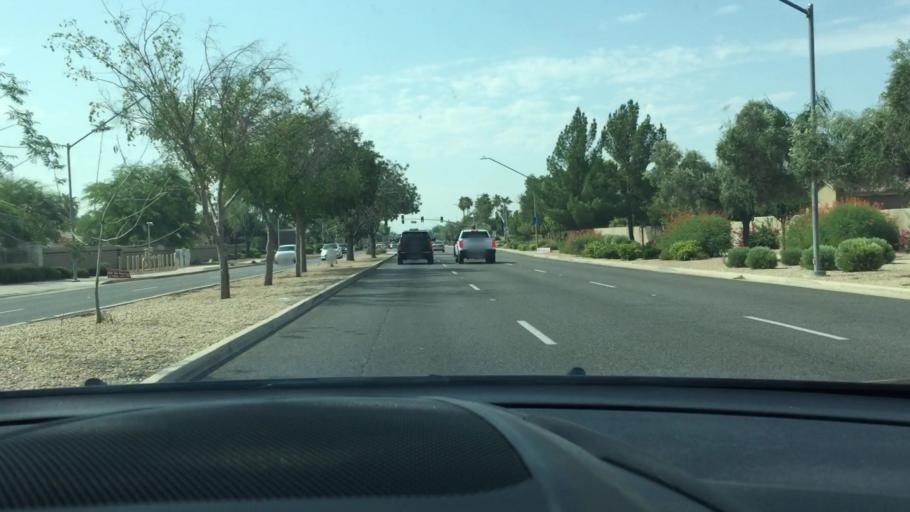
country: US
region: Arizona
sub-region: Maricopa County
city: Peoria
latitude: 33.6736
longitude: -112.2031
